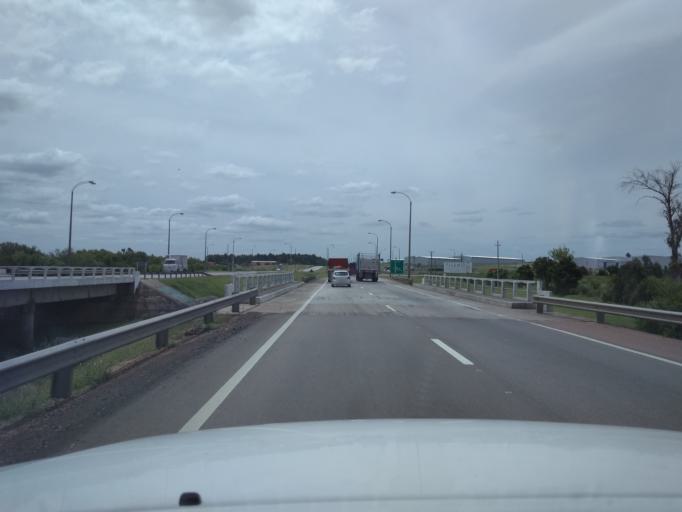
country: UY
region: Canelones
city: Progreso
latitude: -34.6927
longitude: -56.2384
